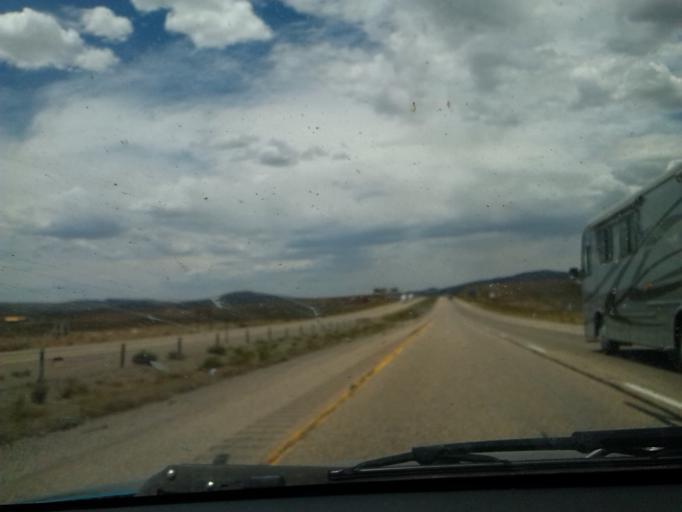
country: US
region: Wyoming
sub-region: Carbon County
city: Rawlins
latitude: 41.7831
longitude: -107.1526
